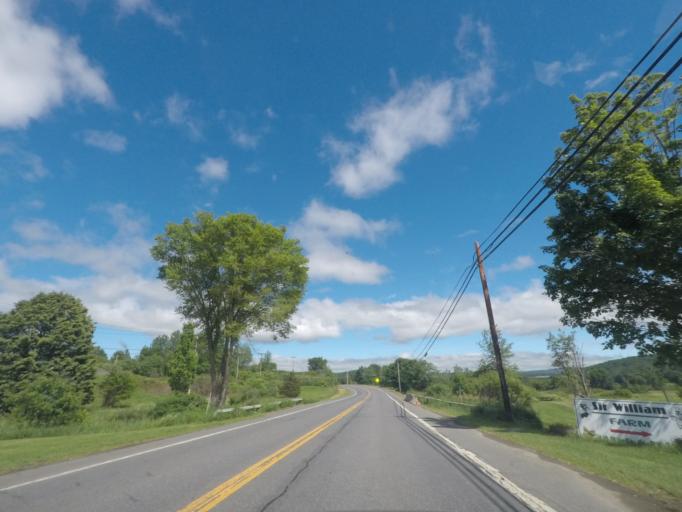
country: US
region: New York
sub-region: Columbia County
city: Philmont
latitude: 42.1745
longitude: -73.5917
